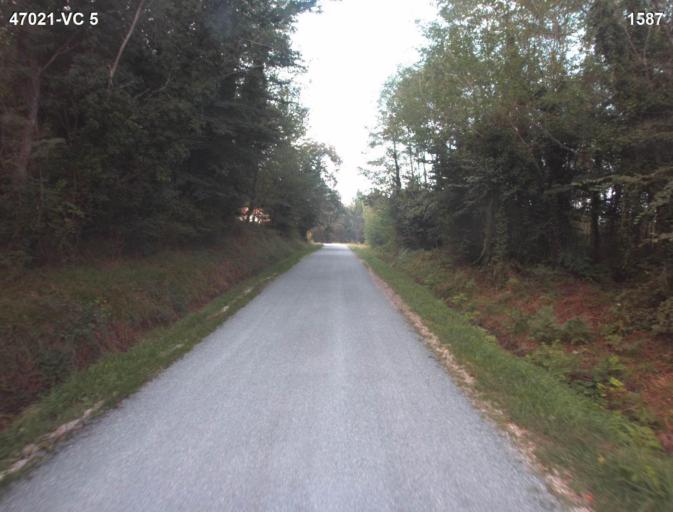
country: FR
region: Aquitaine
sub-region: Departement du Lot-et-Garonne
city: Barbaste
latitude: 44.1429
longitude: 0.2783
